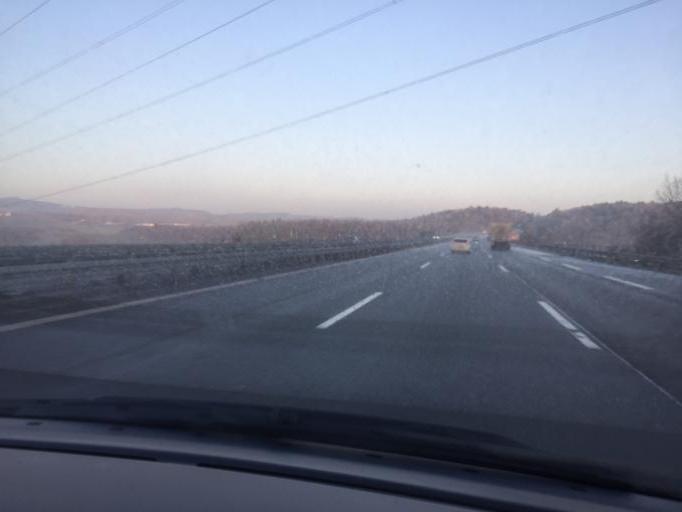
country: DE
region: Baden-Wuerttemberg
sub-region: Freiburg Region
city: Engen
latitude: 47.8670
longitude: 8.7815
